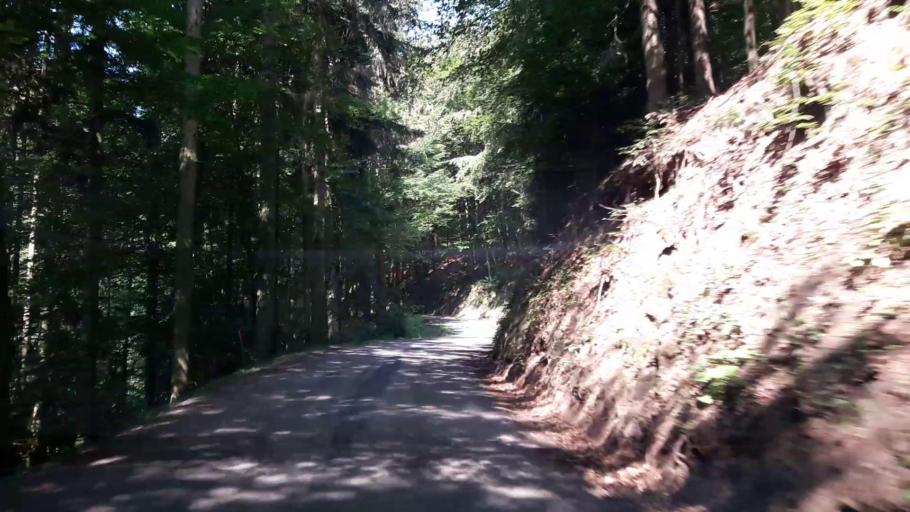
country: AT
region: Lower Austria
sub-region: Politischer Bezirk Krems
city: Aggsbach
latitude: 48.2892
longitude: 15.3757
